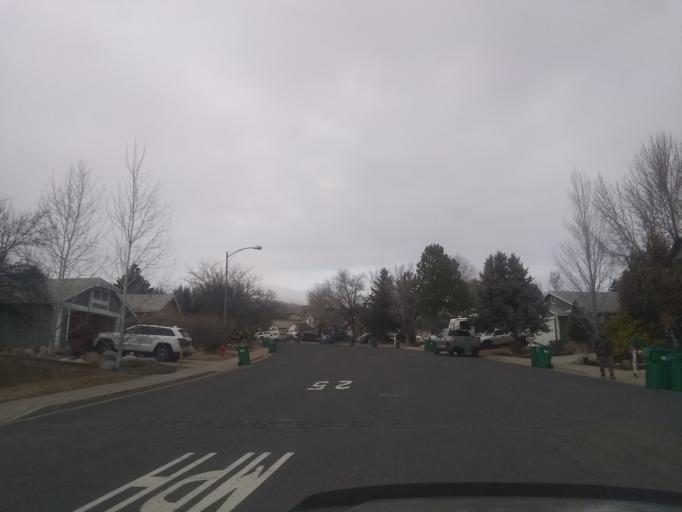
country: US
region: Nevada
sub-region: Washoe County
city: Mogul
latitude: 39.5235
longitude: -119.8844
